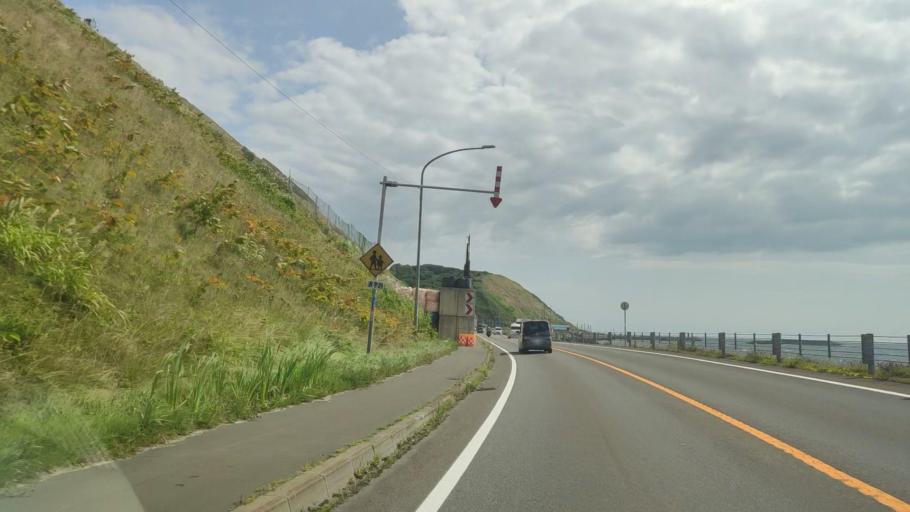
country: JP
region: Hokkaido
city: Rumoi
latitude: 44.2333
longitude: 141.6564
